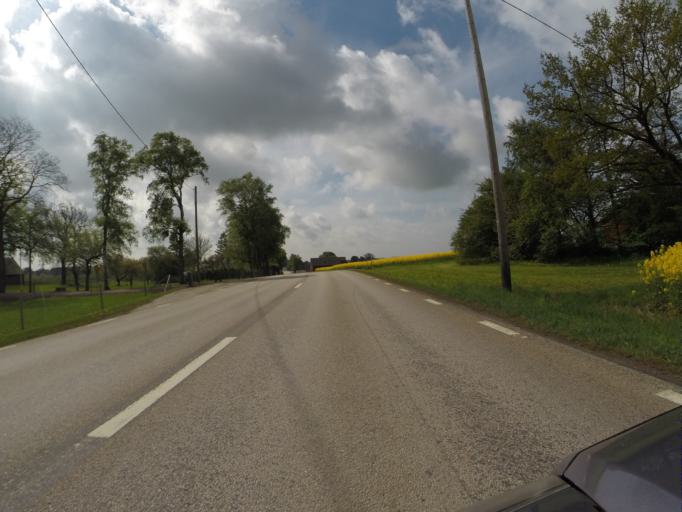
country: SE
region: Skane
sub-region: Landskrona
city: Asmundtorp
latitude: 55.9515
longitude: 12.9467
